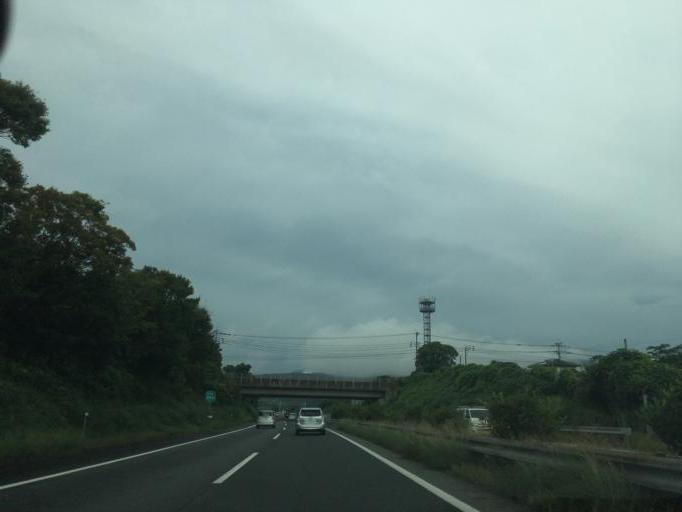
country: JP
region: Saga Prefecture
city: Tosu
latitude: 33.3972
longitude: 130.5146
